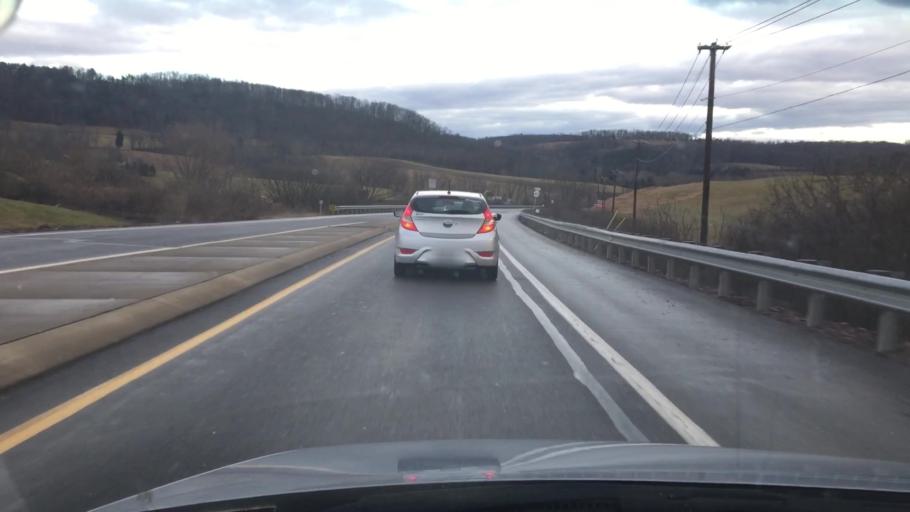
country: US
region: Pennsylvania
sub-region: Columbia County
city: Bloomsburg
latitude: 41.0197
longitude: -76.4893
